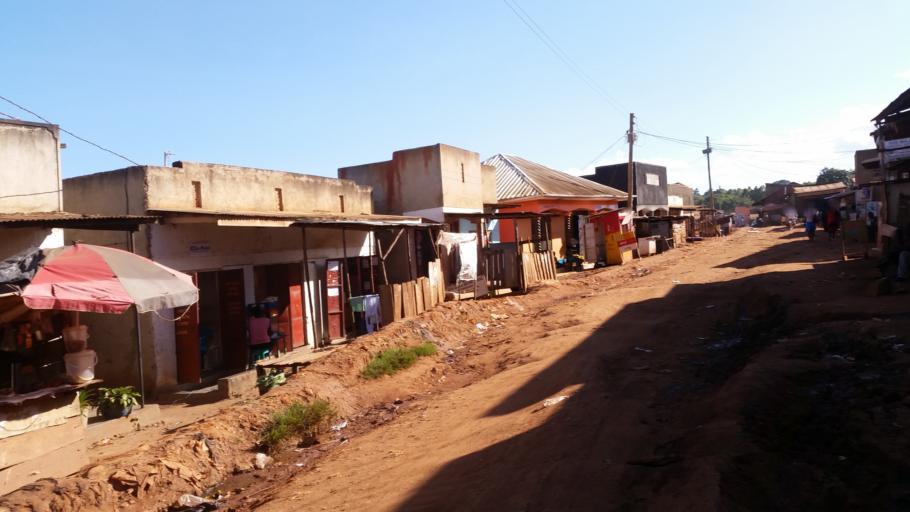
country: UG
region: Central Region
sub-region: Wakiso District
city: Kireka
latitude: 0.3283
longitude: 32.6483
